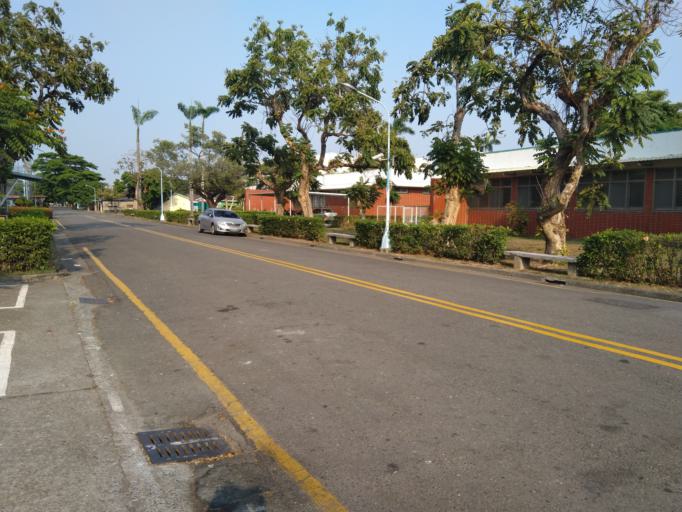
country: TW
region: Kaohsiung
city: Kaohsiung
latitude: 22.7150
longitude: 120.3046
